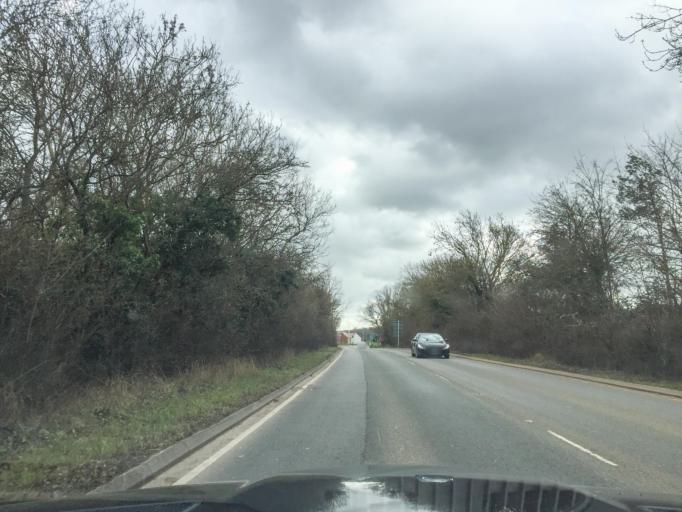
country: GB
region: England
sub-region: Warwickshire
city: Wellesbourne Mountford
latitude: 52.1869
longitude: -1.5982
